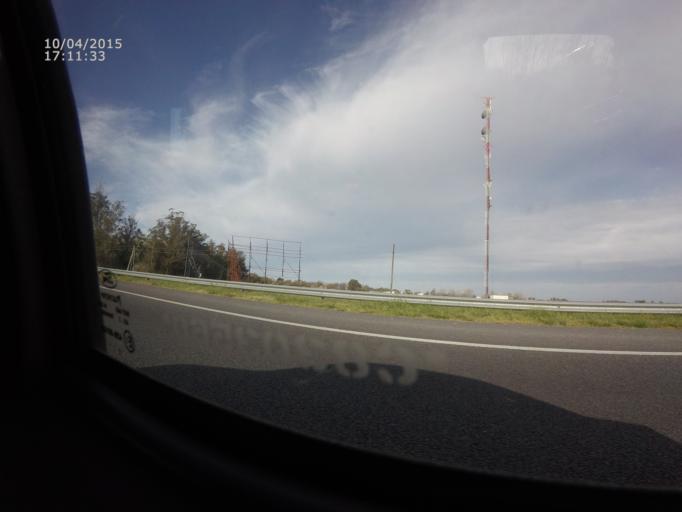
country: AR
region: Buenos Aires
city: Coronel Vidal
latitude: -37.2804
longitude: -57.7653
